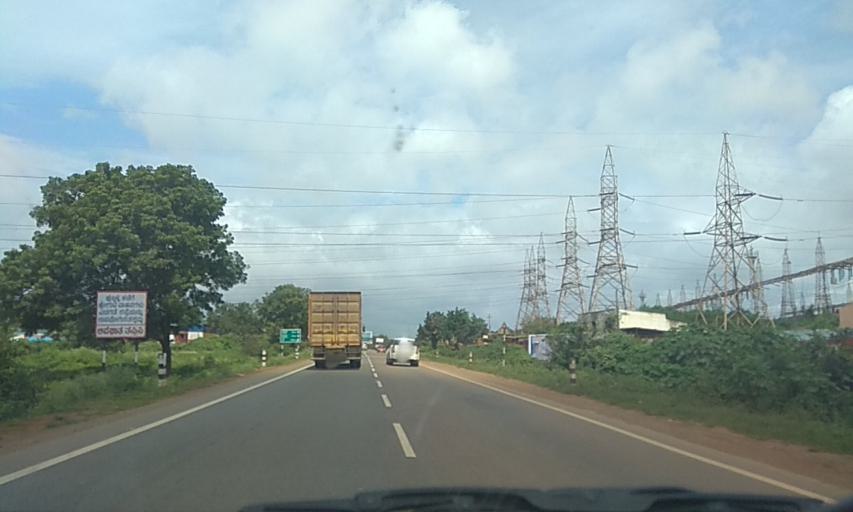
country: IN
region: Karnataka
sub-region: Dharwad
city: Hubli
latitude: 15.3262
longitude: 75.1238
